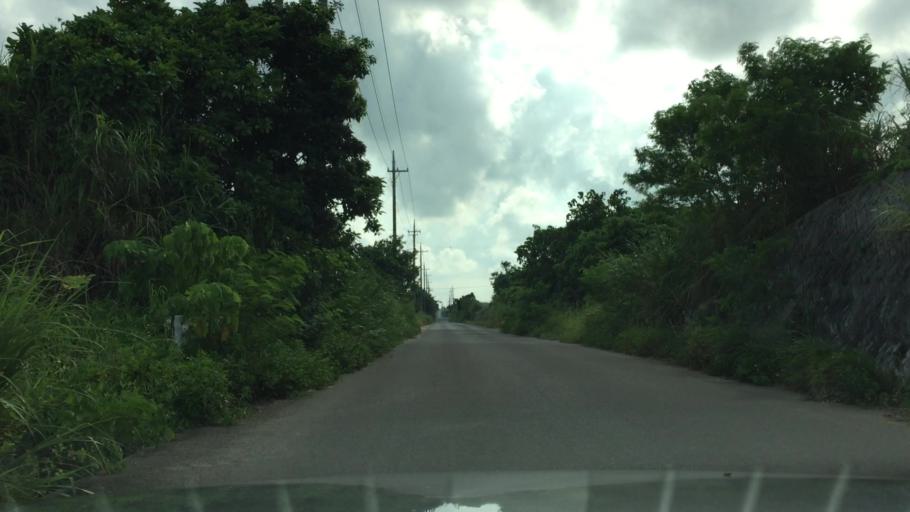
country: JP
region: Okinawa
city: Ishigaki
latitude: 24.3984
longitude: 124.1983
